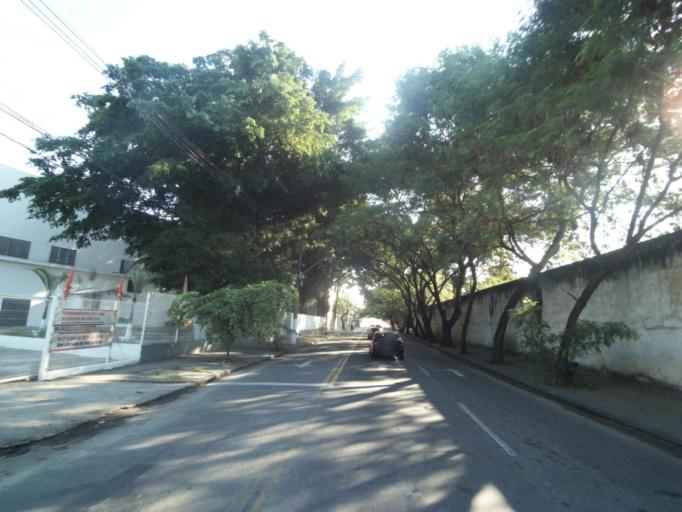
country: BR
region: Rio de Janeiro
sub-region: Niteroi
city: Niteroi
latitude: -22.8850
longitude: -43.1179
